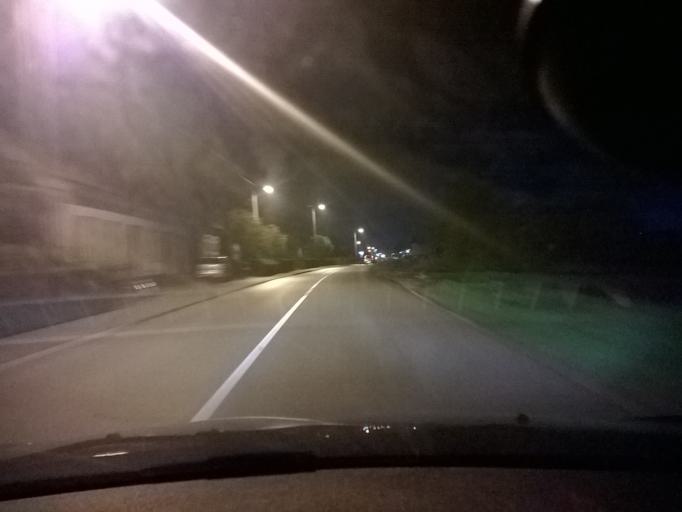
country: HR
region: Krapinsko-Zagorska
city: Zabok
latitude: 46.0207
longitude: 15.8935
